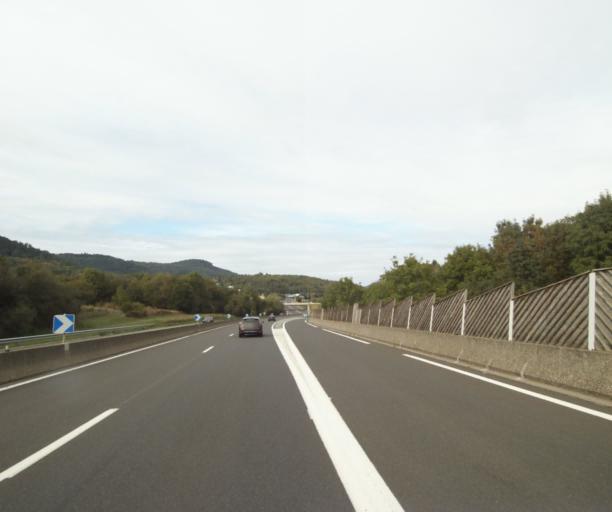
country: FR
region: Auvergne
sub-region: Departement du Puy-de-Dome
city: Ceyrat
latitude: 45.7276
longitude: 3.0708
